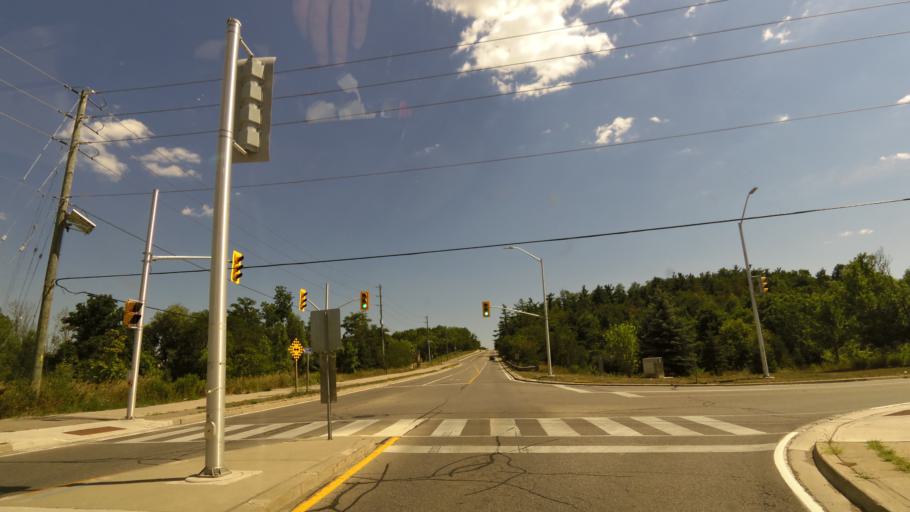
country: CA
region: Ontario
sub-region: Halton
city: Milton
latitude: 43.6367
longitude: -79.9092
